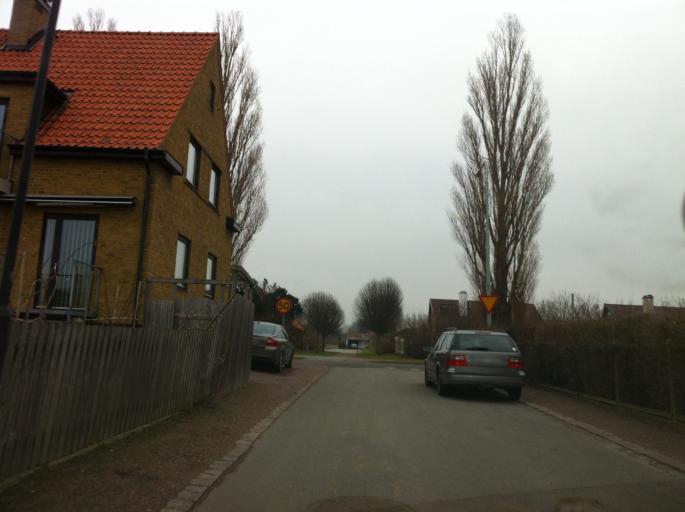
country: SE
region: Skane
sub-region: Landskrona
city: Landskrona
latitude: 55.8928
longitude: 12.8089
